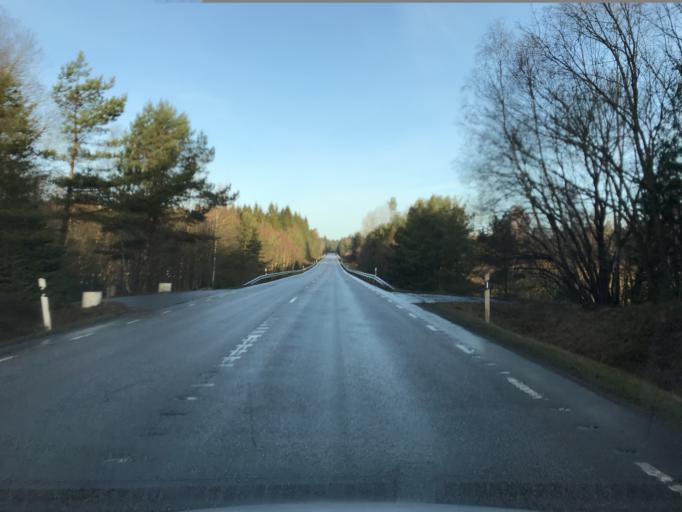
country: SE
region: Skane
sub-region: Hassleholms Kommun
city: Bjarnum
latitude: 56.2247
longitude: 13.7224
